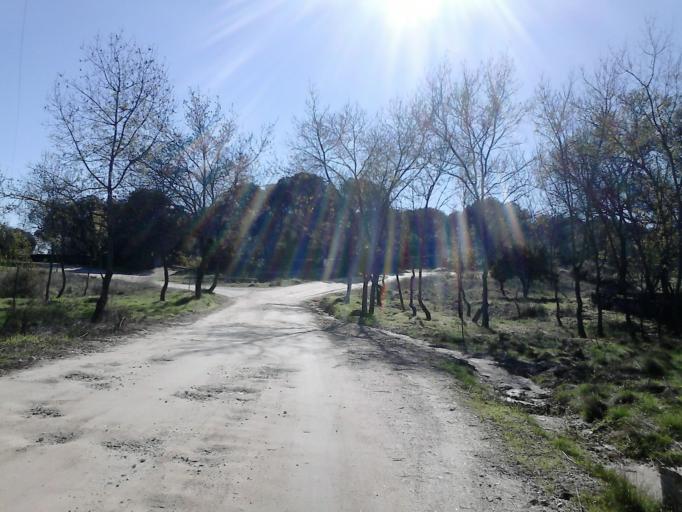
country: ES
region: Madrid
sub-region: Provincia de Madrid
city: Galapagar
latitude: 40.5648
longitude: -3.9776
